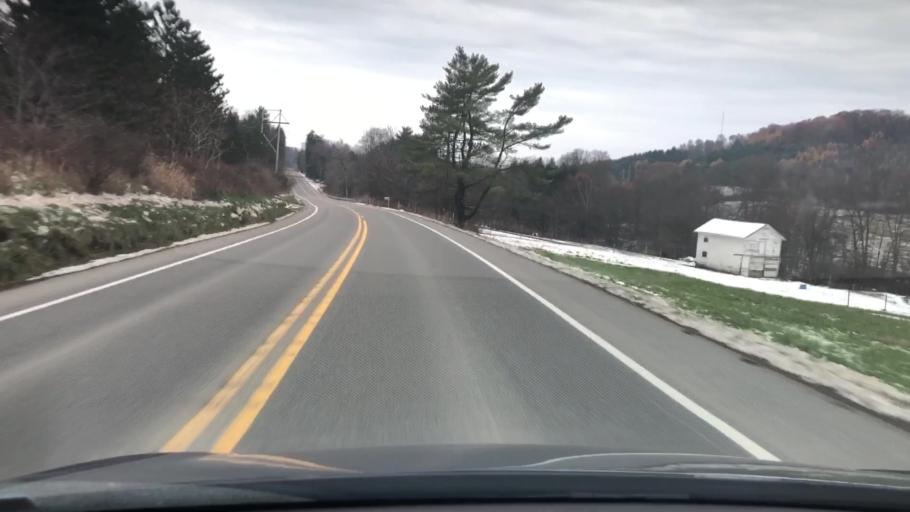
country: US
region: Pennsylvania
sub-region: Jefferson County
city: Brookville
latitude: 41.0528
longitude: -79.2518
